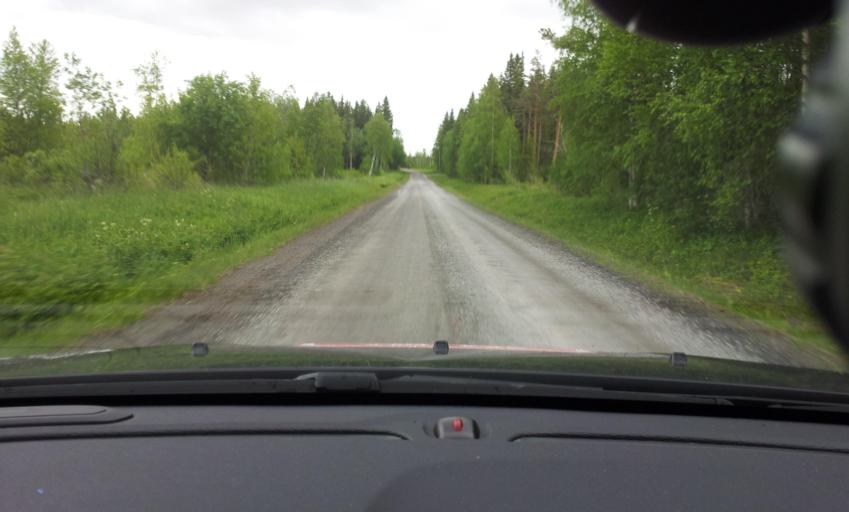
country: SE
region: Jaemtland
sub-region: OEstersunds Kommun
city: Brunflo
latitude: 63.1519
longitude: 15.0195
